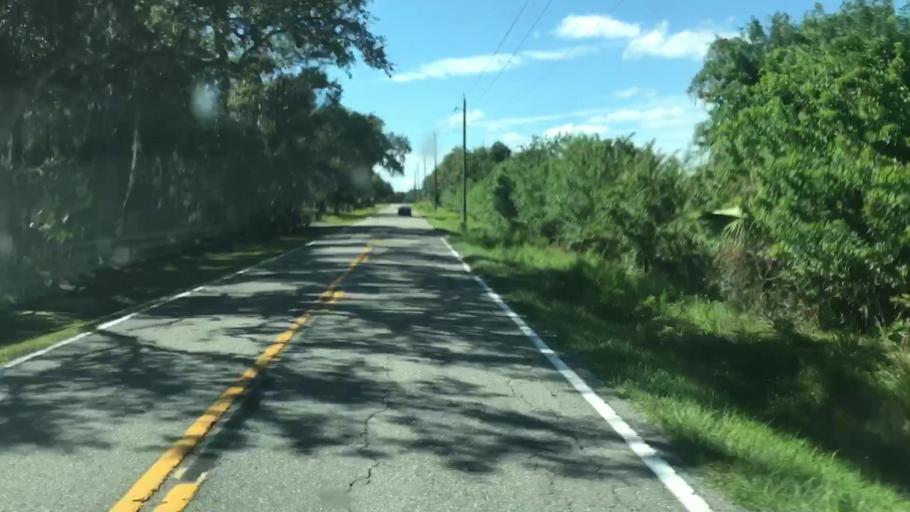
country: US
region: Florida
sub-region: Lee County
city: Olga
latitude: 26.7307
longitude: -81.7040
